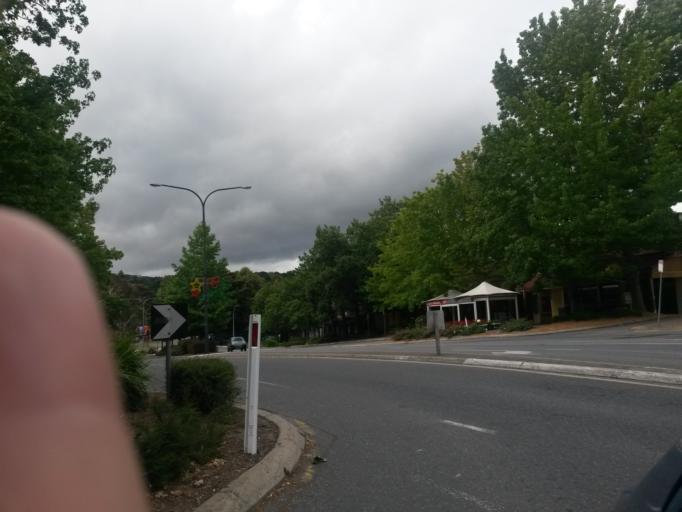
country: AU
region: South Australia
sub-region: Adelaide Hills
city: Heathfield
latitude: -35.0046
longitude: 138.7163
